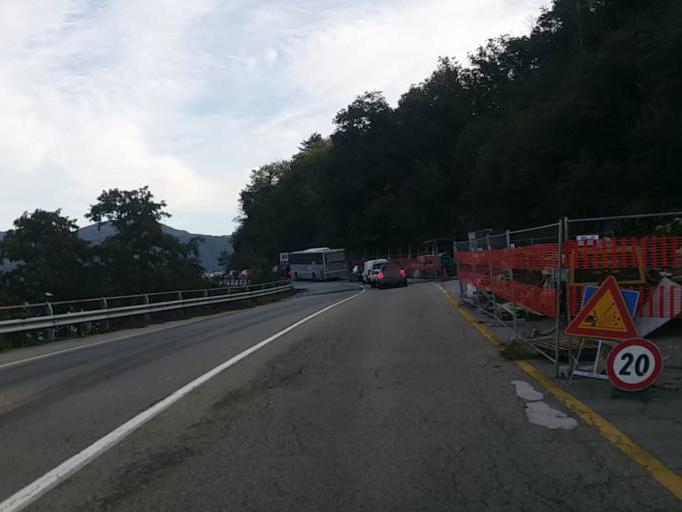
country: IT
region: Lombardy
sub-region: Provincia di Varese
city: Maccagno
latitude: 46.0373
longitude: 8.7091
